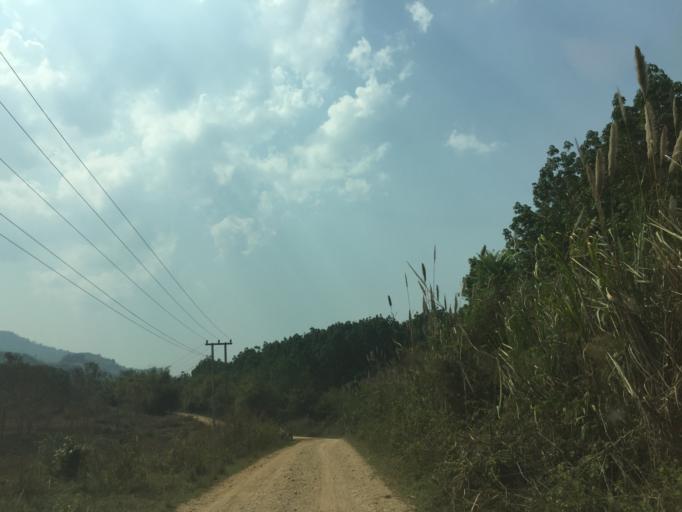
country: TH
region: Nan
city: Thung Chang
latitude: 19.7317
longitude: 100.7348
